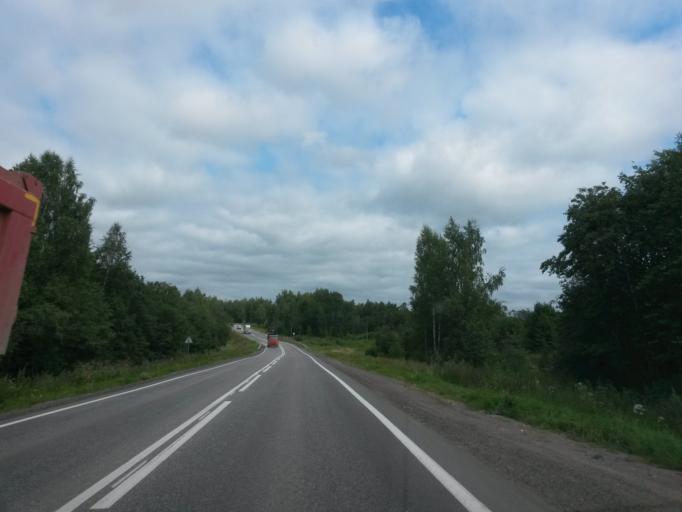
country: RU
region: Jaroslavl
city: Gavrilov-Yam
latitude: 57.3337
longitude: 39.9208
